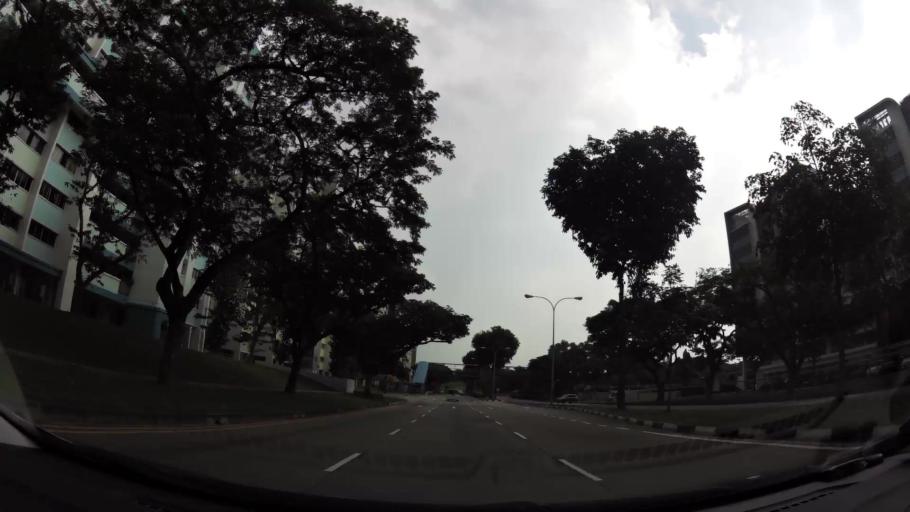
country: SG
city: Singapore
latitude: 1.3460
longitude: 103.9352
